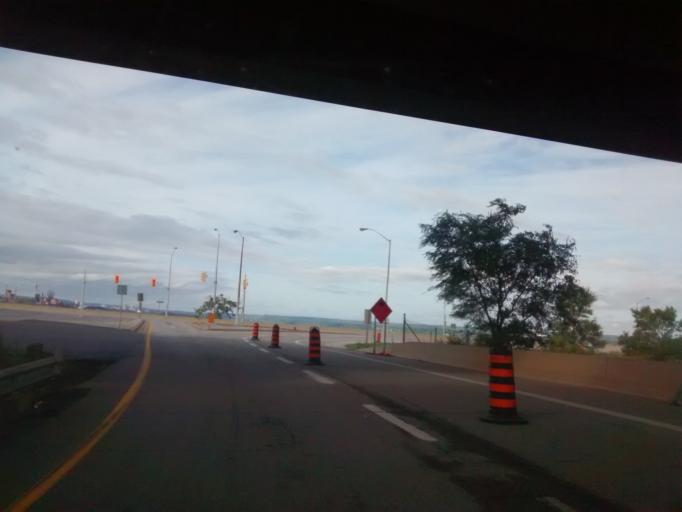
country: CA
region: Ontario
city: Hamilton
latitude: 43.2900
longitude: -79.7923
